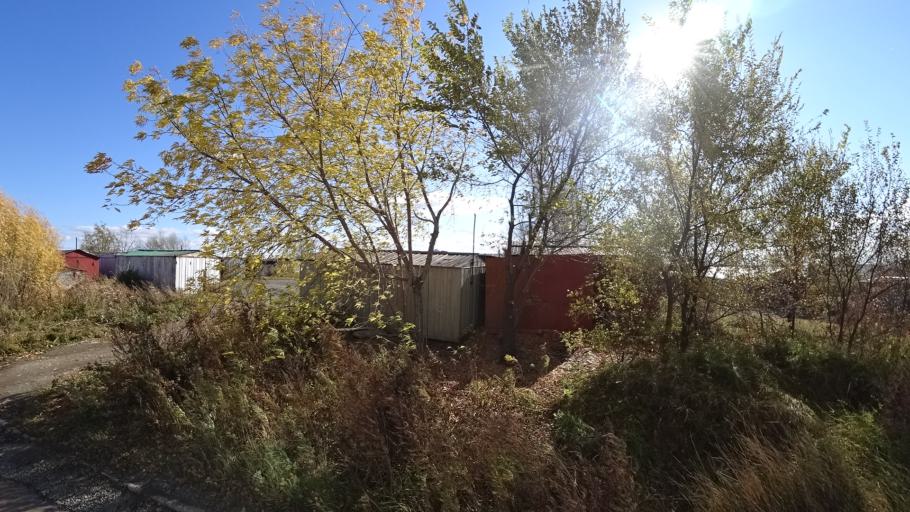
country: RU
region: Khabarovsk Krai
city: Amursk
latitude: 50.2159
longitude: 136.8893
